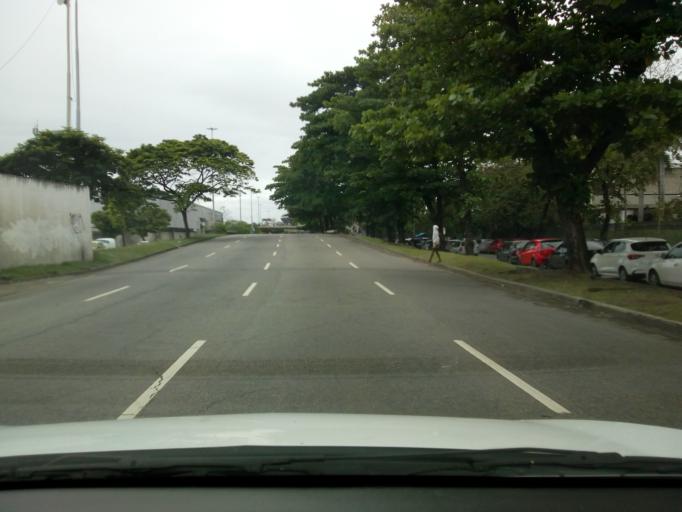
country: BR
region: Rio de Janeiro
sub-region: Rio De Janeiro
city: Rio de Janeiro
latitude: -22.9097
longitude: -43.2365
